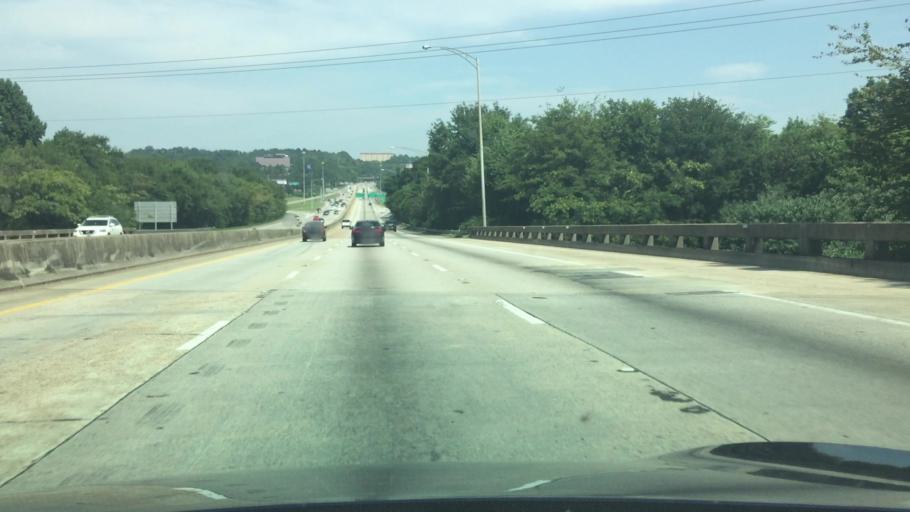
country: US
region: Alabama
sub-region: Jefferson County
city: Homewood
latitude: 33.4584
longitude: -86.8203
